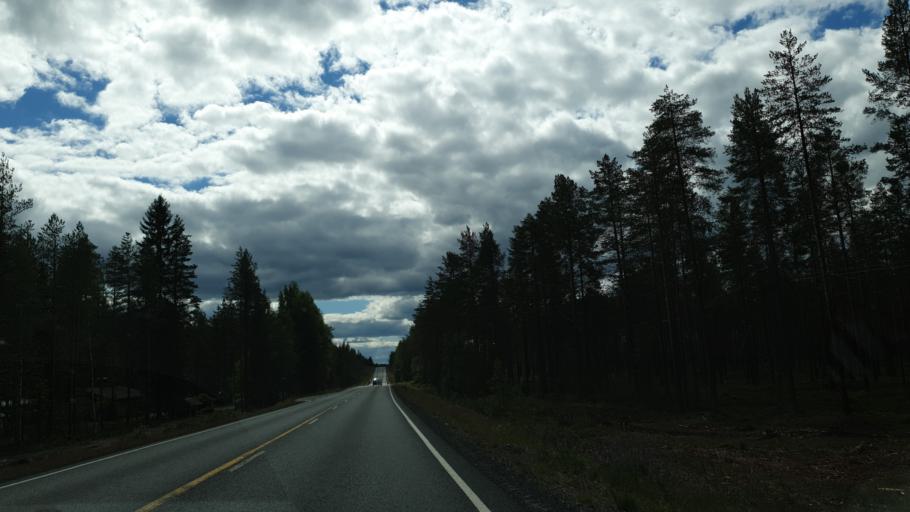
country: FI
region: Kainuu
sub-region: Kehys-Kainuu
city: Kuhmo
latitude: 64.0899
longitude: 29.4813
